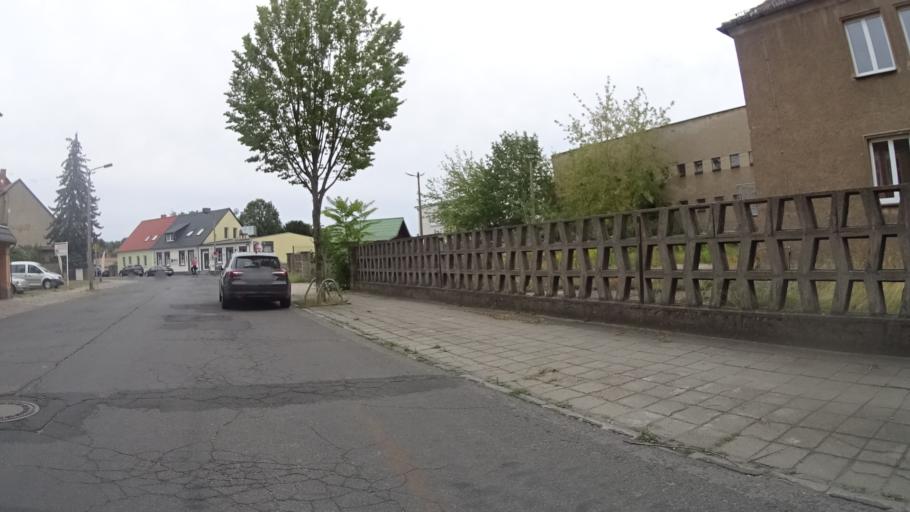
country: DE
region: Brandenburg
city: Luckenwalde
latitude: 52.0838
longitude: 13.1605
